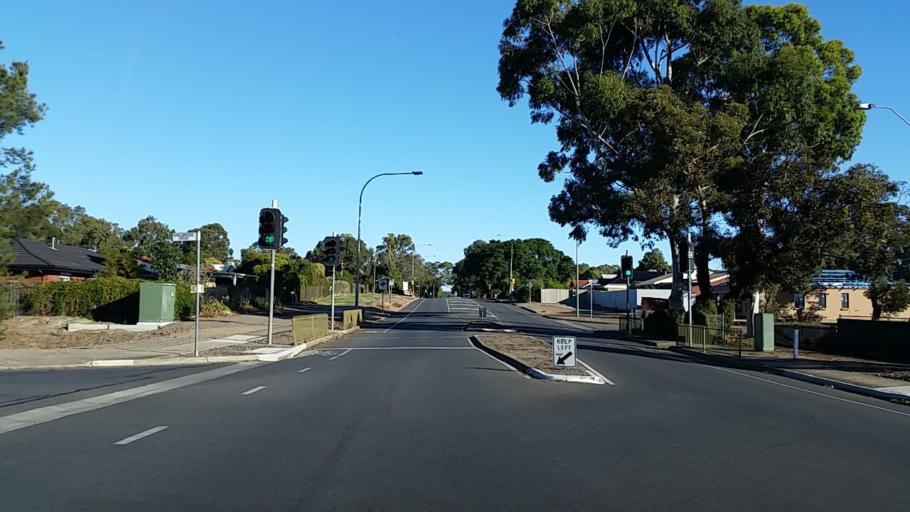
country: AU
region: South Australia
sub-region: Onkaparinga
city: Morphett Vale
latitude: -35.1190
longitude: 138.5359
